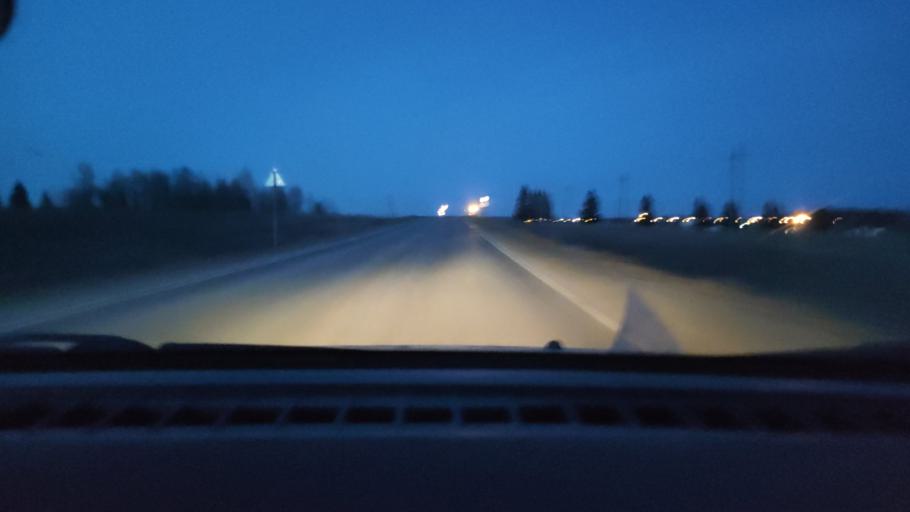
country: RU
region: Perm
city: Lobanovo
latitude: 57.8066
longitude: 56.2971
